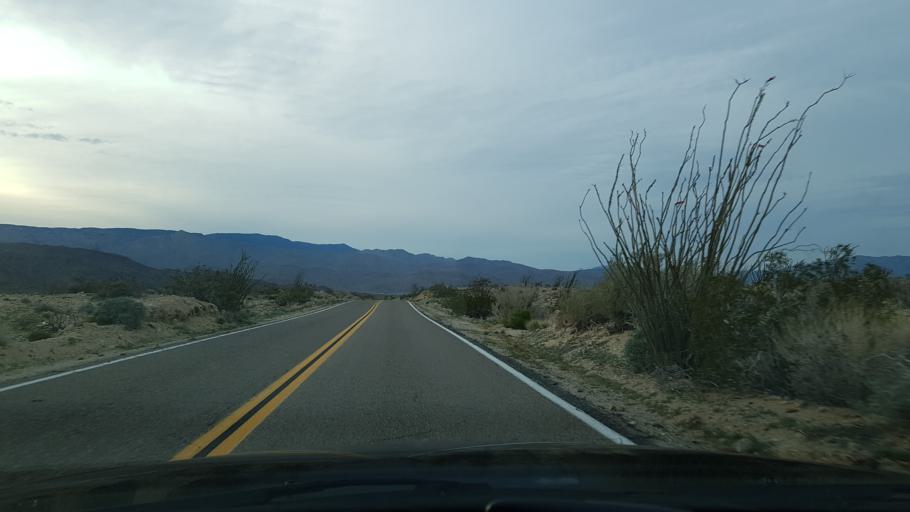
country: MX
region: Baja California
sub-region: Tecate
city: Cereso del Hongo
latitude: 32.8212
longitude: -116.1539
